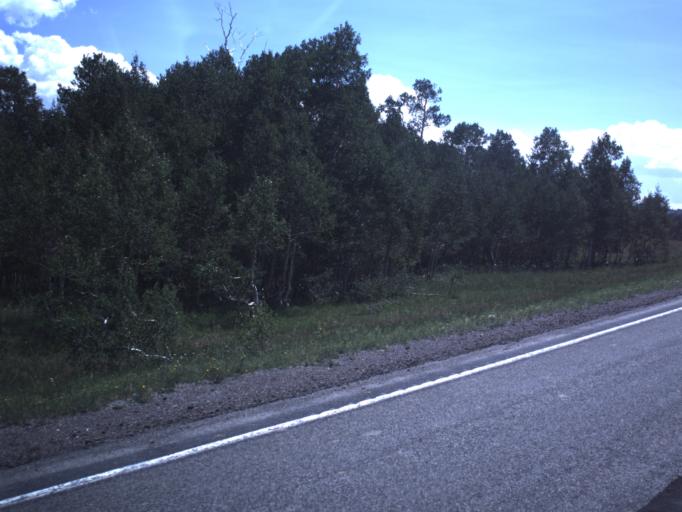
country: US
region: Utah
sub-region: Sanpete County
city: Fairview
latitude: 39.6637
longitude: -111.3290
